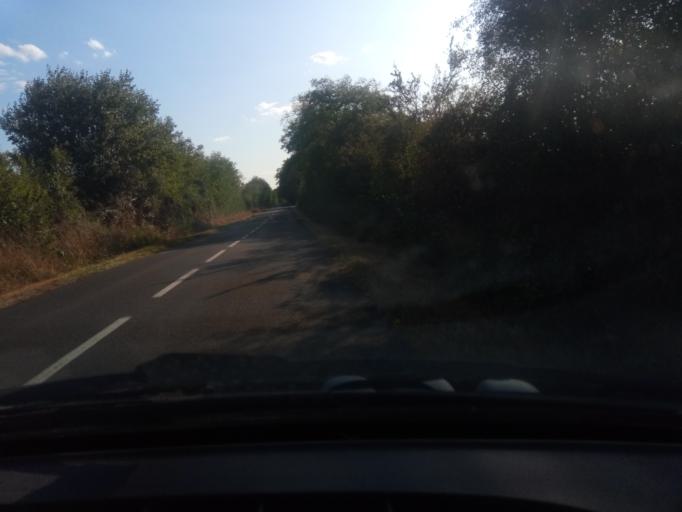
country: FR
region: Poitou-Charentes
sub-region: Departement de la Vienne
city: Lussac-les-Chateaux
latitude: 46.3769
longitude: 0.7096
